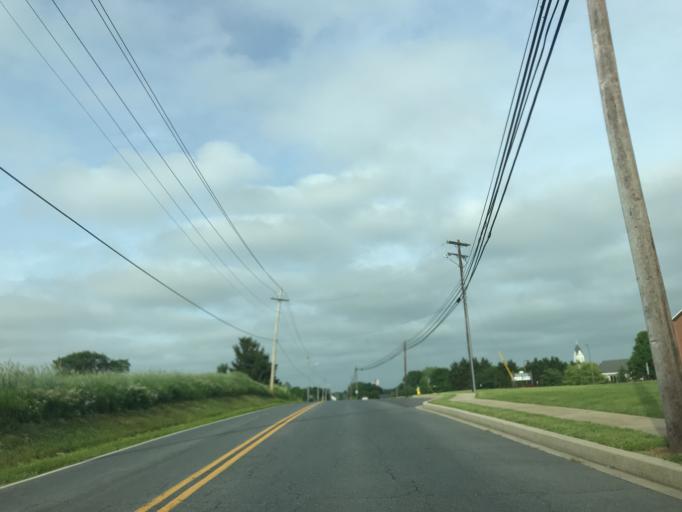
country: US
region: Maryland
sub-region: Frederick County
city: Walkersville
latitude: 39.4821
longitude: -77.3684
